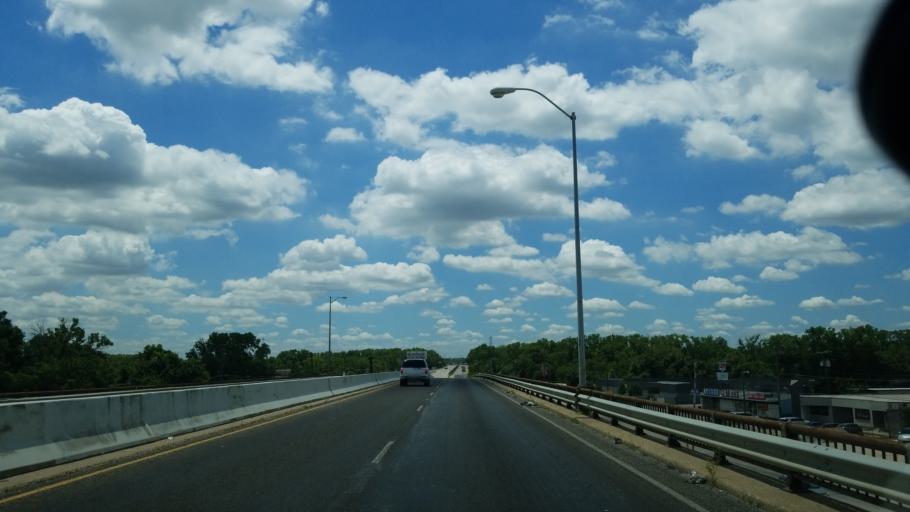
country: US
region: Texas
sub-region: Dallas County
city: Dallas
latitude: 32.7370
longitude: -96.7577
